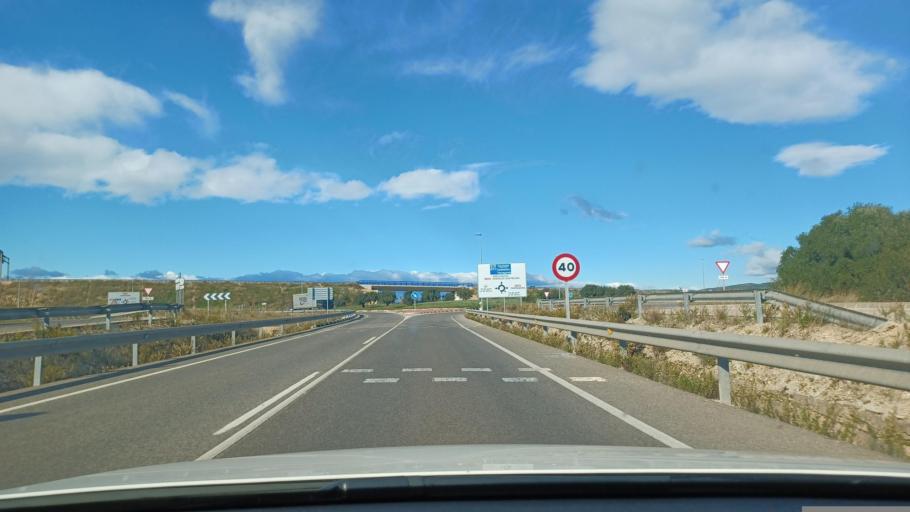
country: ES
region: Valencia
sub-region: Provincia de Castello
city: Vinaros
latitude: 40.4952
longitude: 0.4650
